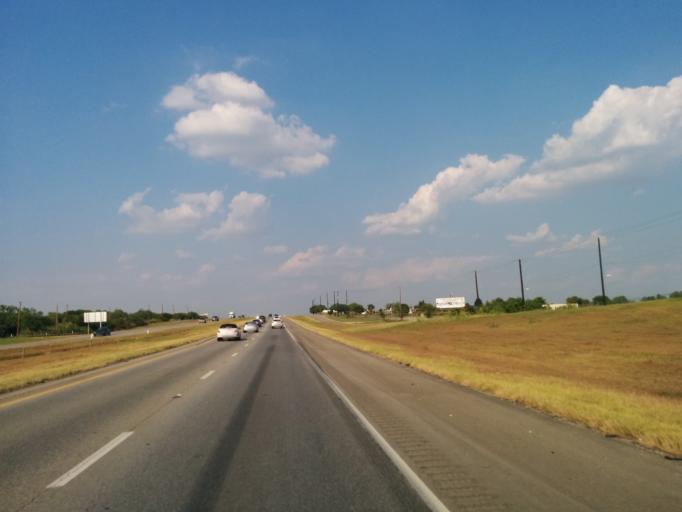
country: US
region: Texas
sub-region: Bexar County
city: Converse
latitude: 29.4742
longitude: -98.2640
